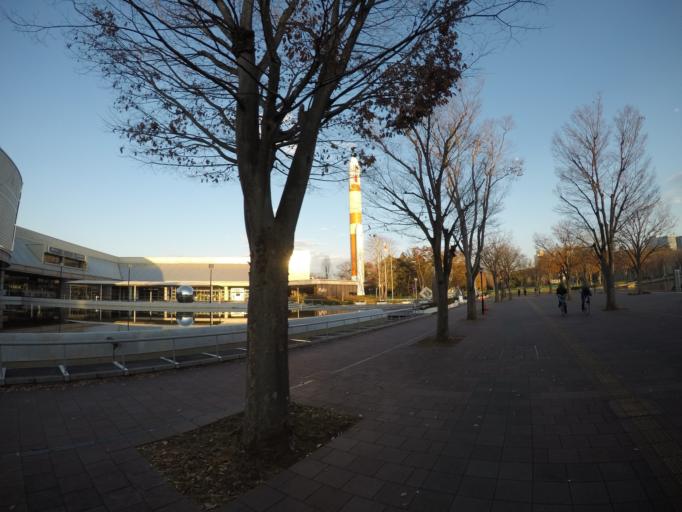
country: JP
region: Ibaraki
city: Naka
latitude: 36.0860
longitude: 140.1101
